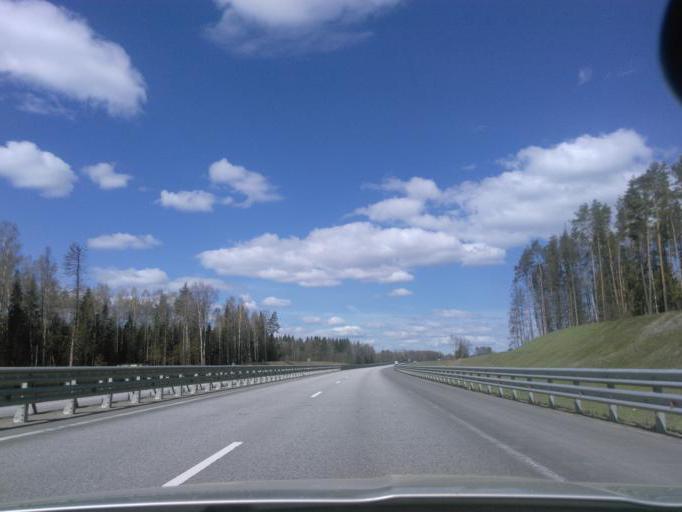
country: RU
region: Moskovskaya
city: Radumlya
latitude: 56.1034
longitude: 37.1442
